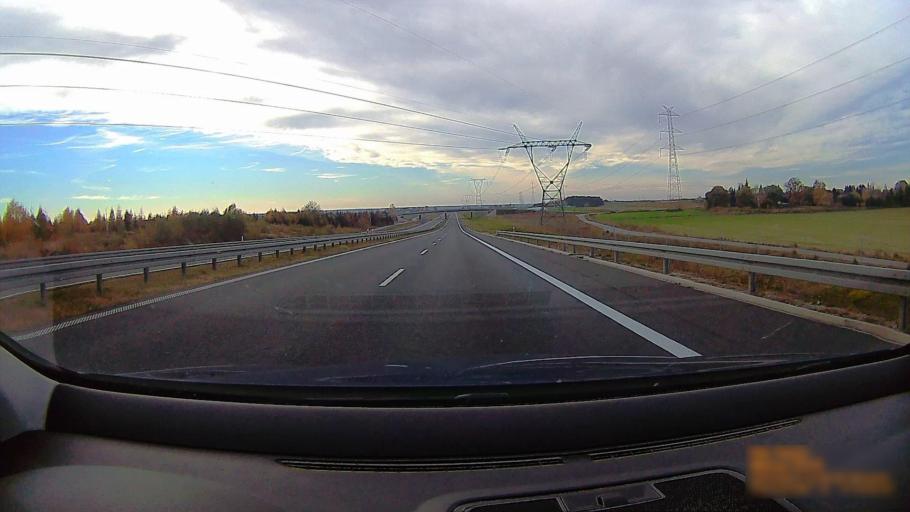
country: PL
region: Greater Poland Voivodeship
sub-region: Powiat ostrowski
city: Przygodzice
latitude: 51.6173
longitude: 17.8602
